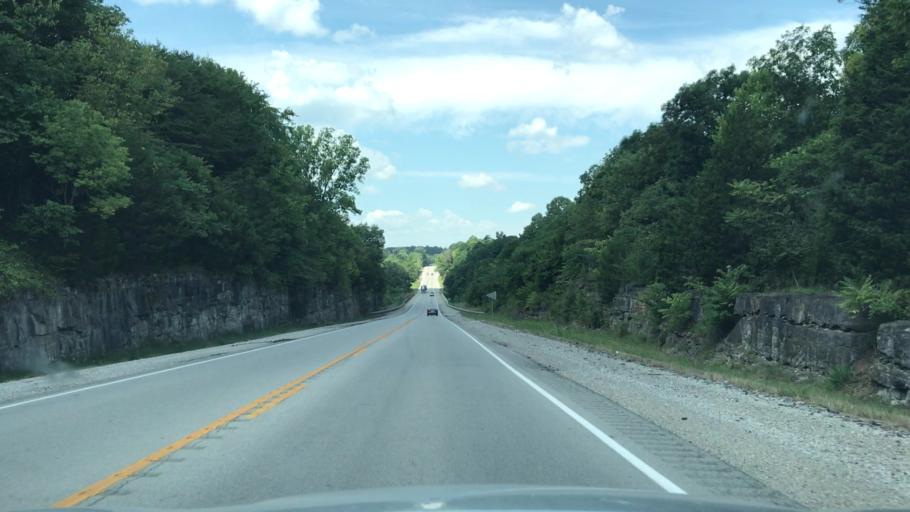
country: US
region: Kentucky
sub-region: Wayne County
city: Monticello
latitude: 36.7653
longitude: -84.9701
